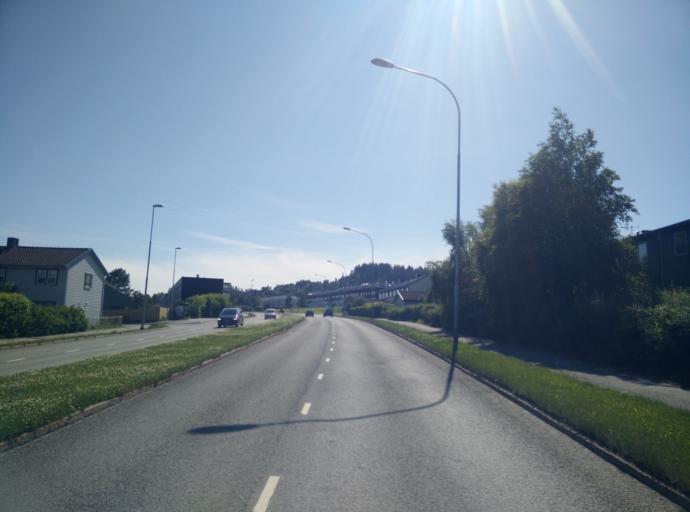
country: NO
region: Sor-Trondelag
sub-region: Trondheim
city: Trondheim
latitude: 63.4130
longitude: 10.3629
